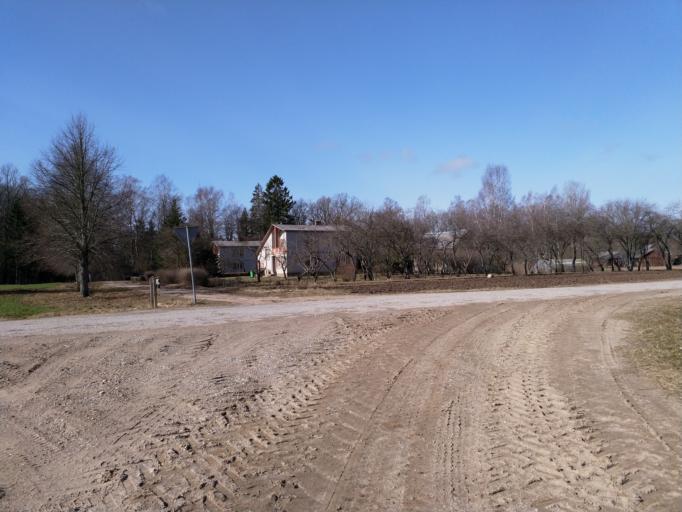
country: LV
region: Aizpute
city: Aizpute
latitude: 56.8302
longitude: 21.7740
